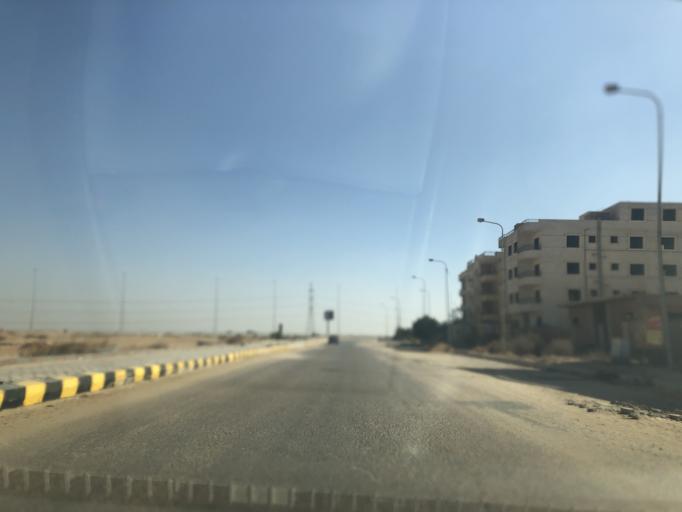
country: EG
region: Al Jizah
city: Madinat Sittah Uktubar
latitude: 29.8997
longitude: 31.0820
